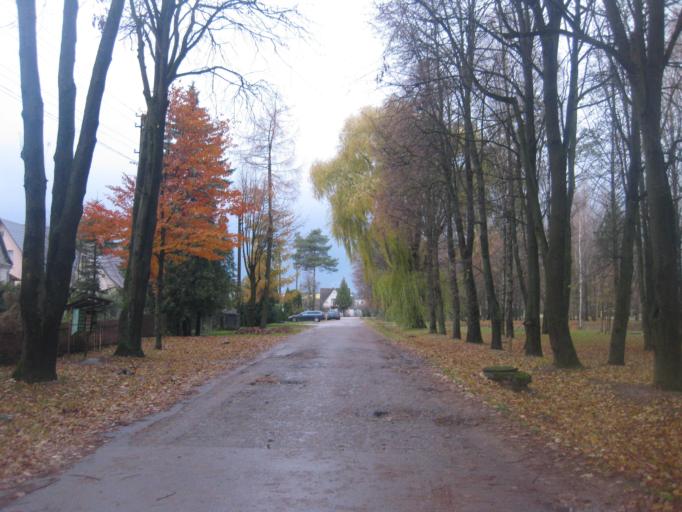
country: LT
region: Kauno apskritis
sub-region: Kaunas
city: Aleksotas
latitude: 54.8585
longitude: 23.8798
